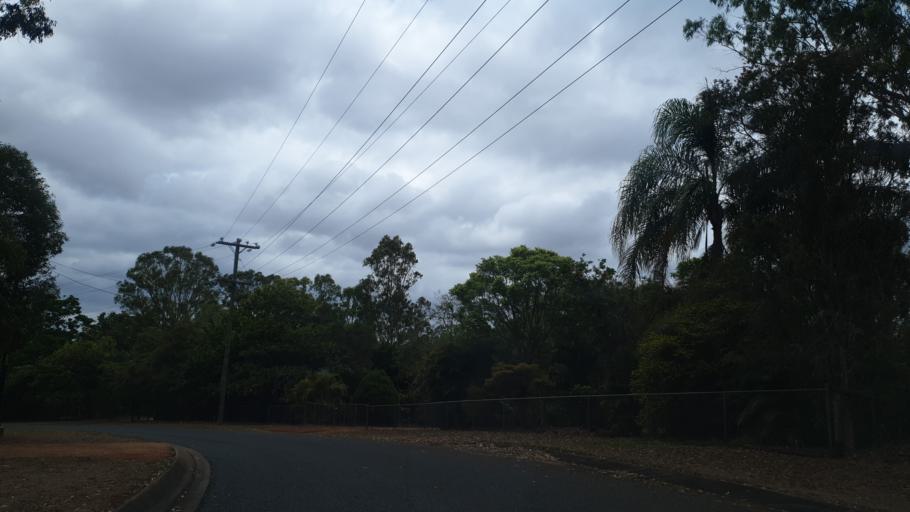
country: AU
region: Queensland
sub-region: Tablelands
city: Tolga
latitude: -17.2084
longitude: 145.4432
